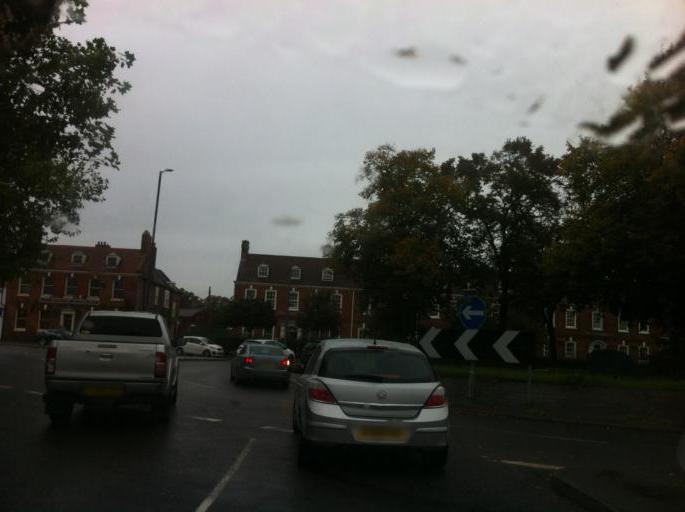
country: GB
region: England
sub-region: Lincolnshire
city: Boston
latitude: 52.9809
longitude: -0.0190
